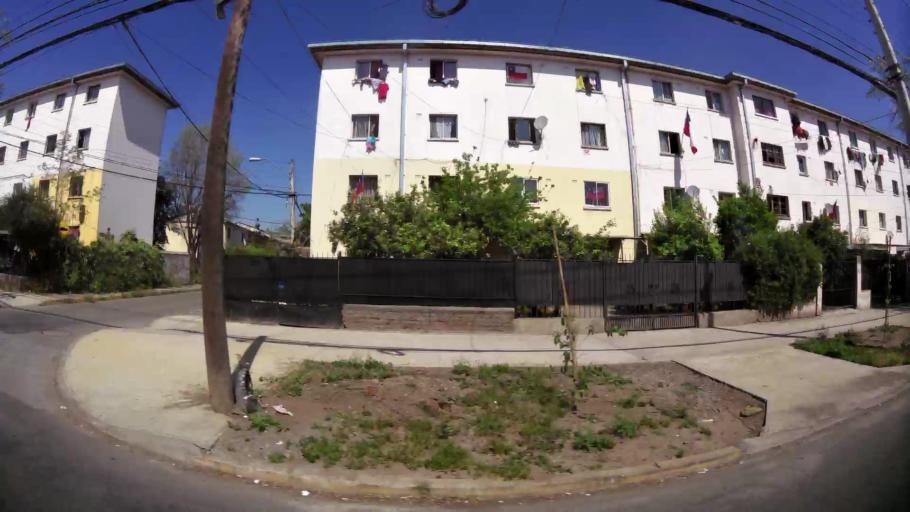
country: CL
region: Santiago Metropolitan
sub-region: Provincia de Santiago
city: Santiago
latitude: -33.4226
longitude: -70.6686
